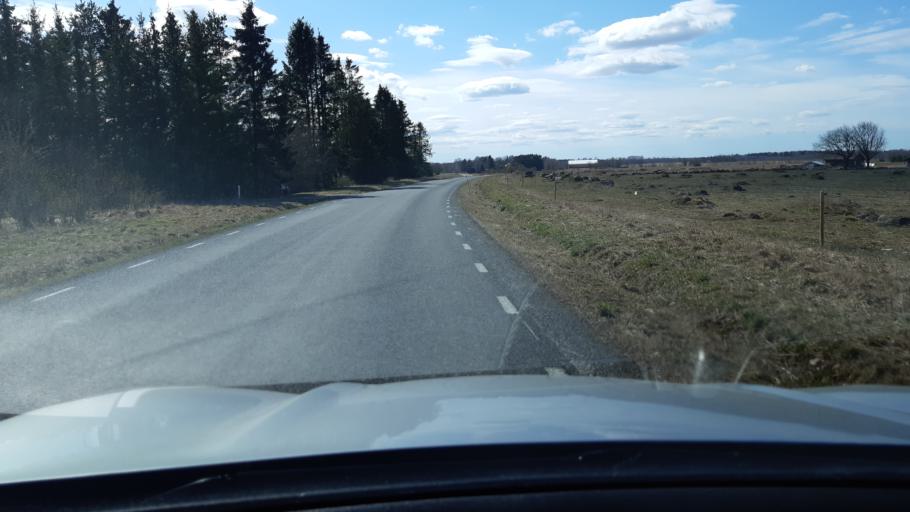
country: EE
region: Raplamaa
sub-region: Kohila vald
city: Kohila
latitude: 59.1850
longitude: 24.8696
